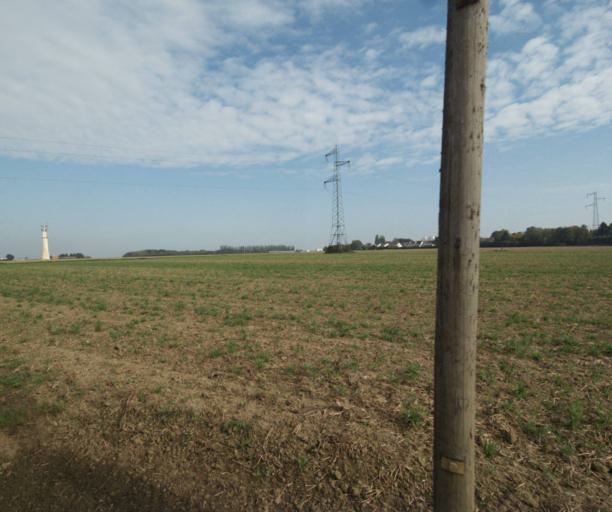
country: FR
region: Nord-Pas-de-Calais
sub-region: Departement du Nord
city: Wattignies
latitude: 50.5853
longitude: 3.0307
